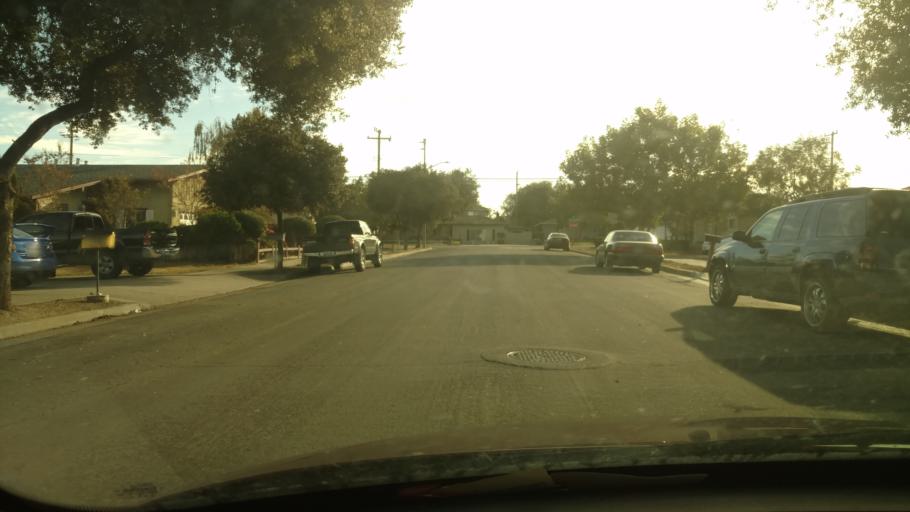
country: US
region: California
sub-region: San Benito County
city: Ridgemark
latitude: 36.8325
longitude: -121.3824
